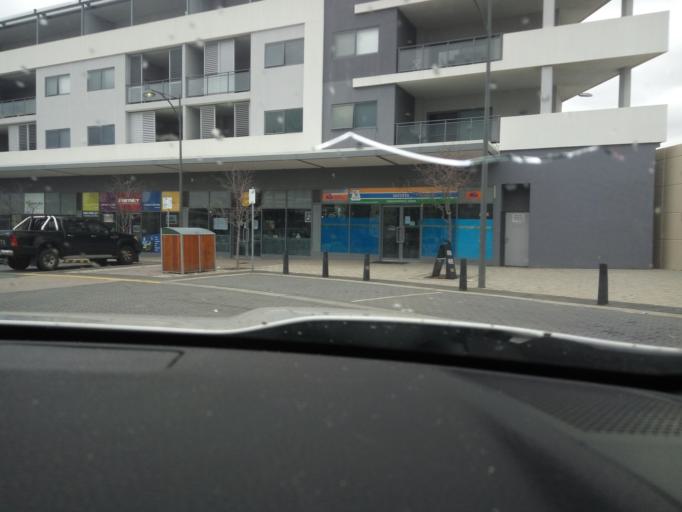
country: AU
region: Western Australia
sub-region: City of Cockburn
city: Success
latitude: -32.1257
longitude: 115.8574
